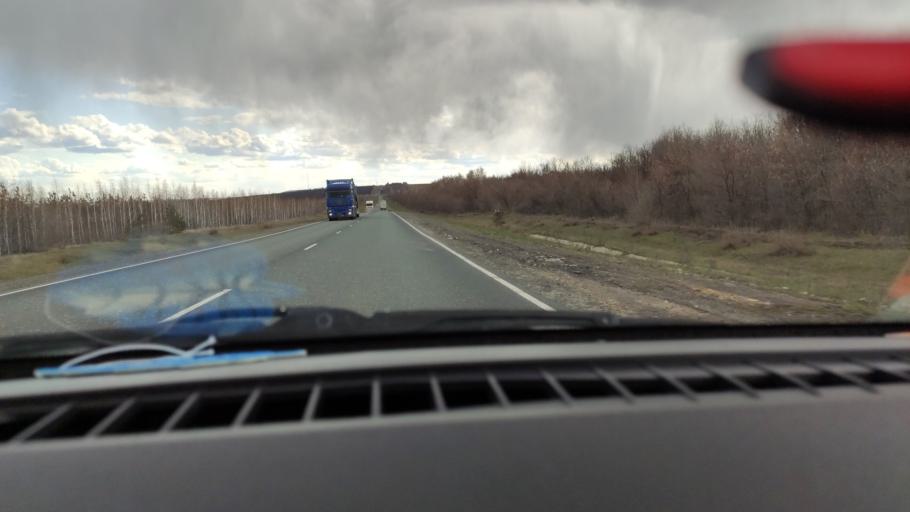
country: RU
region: Saratov
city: Balakovo
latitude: 52.1485
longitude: 47.8089
